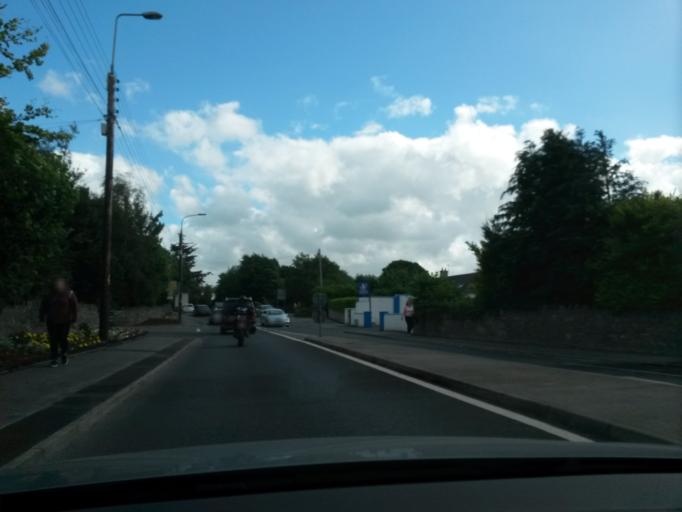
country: IE
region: Munster
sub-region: An Clar
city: Ennis
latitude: 52.8490
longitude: -8.9727
